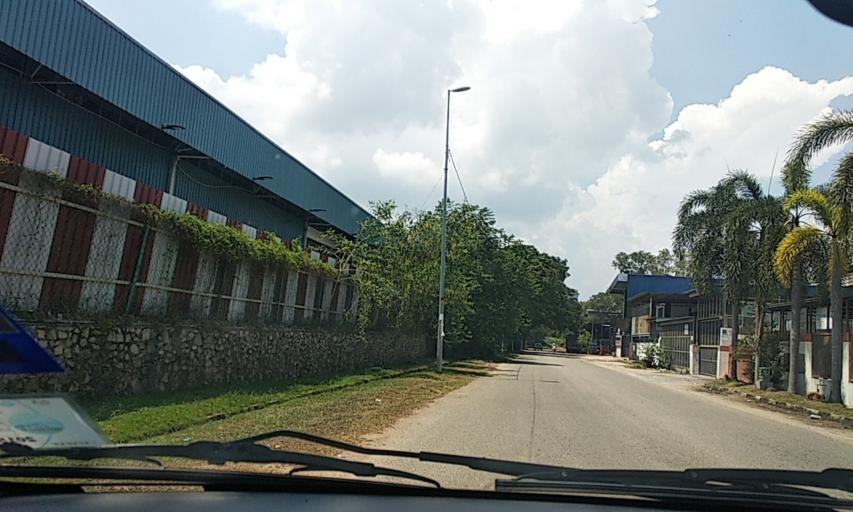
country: MY
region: Kedah
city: Sungai Petani
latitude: 5.6242
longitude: 100.4727
